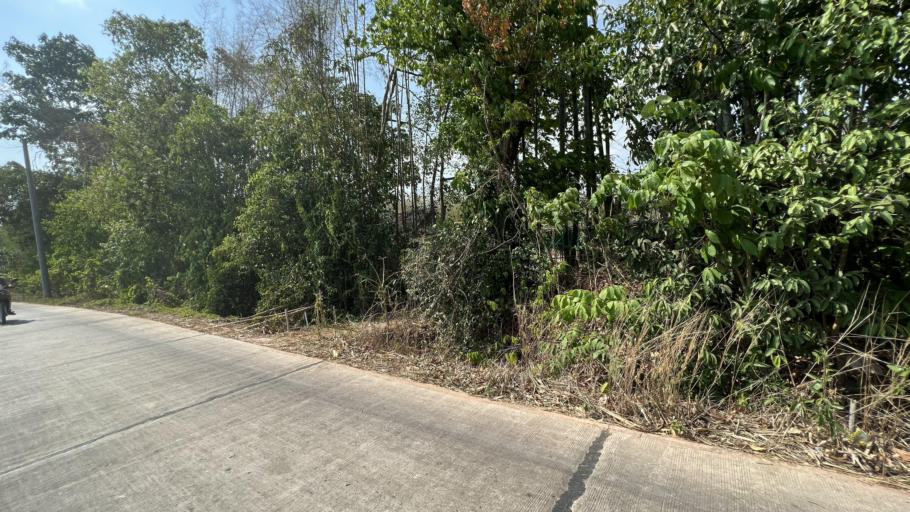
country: MM
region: Yangon
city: Twante
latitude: 16.6587
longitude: 95.9459
